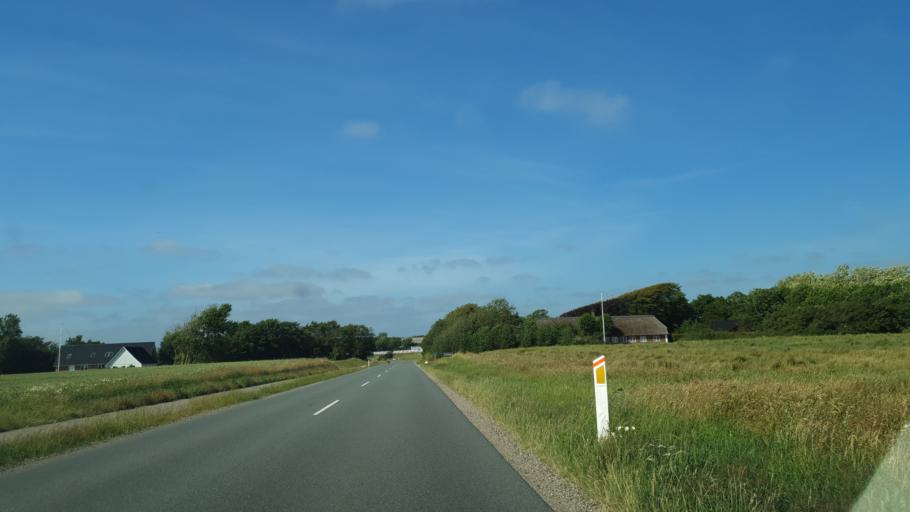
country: DK
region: Central Jutland
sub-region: Ringkobing-Skjern Kommune
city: Ringkobing
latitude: 56.0568
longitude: 8.3130
